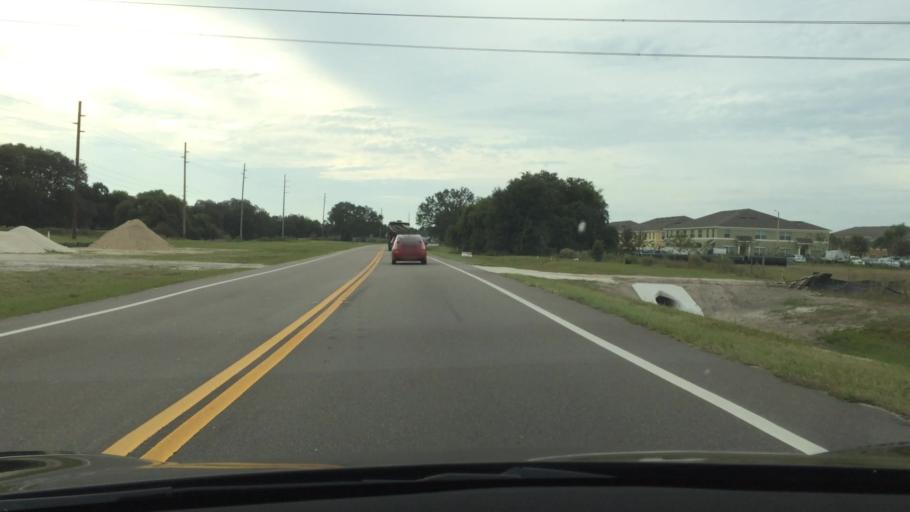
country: US
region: Florida
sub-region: Pasco County
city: Trinity
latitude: 28.1802
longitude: -82.6533
